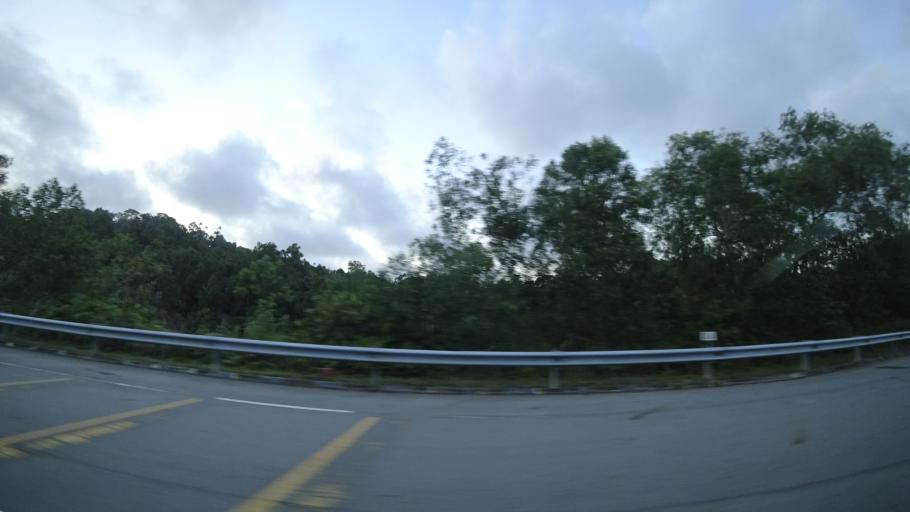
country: BN
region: Brunei and Muara
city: Bandar Seri Begawan
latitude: 4.9079
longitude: 114.8003
